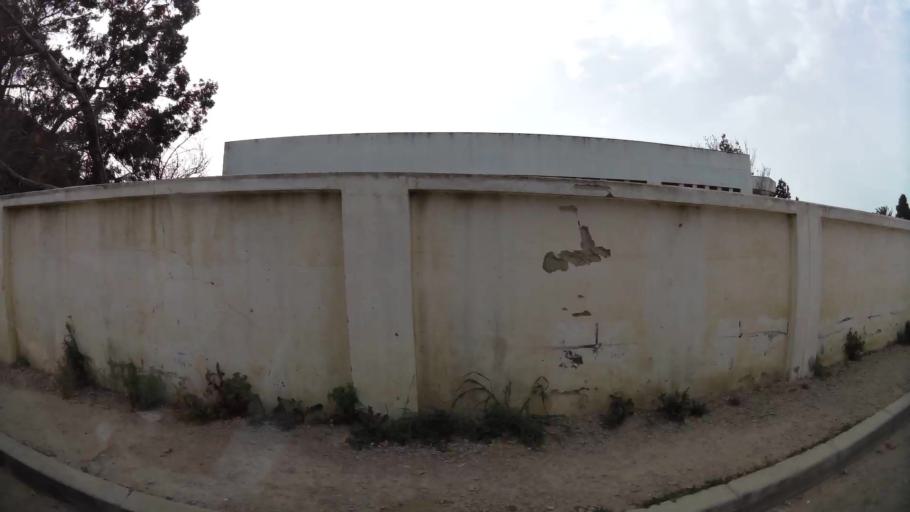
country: MA
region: Tanger-Tetouan
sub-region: Tanger-Assilah
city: Boukhalef
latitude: 35.7023
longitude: -5.8997
